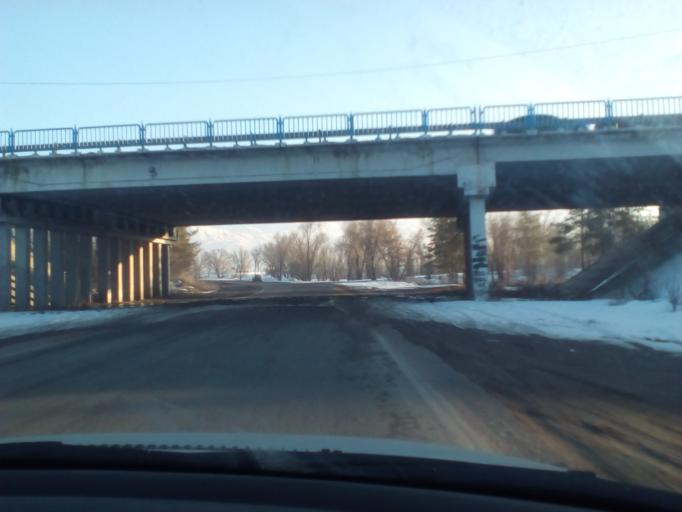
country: KZ
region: Almaty Oblysy
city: Burunday
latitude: 43.2233
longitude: 76.4086
